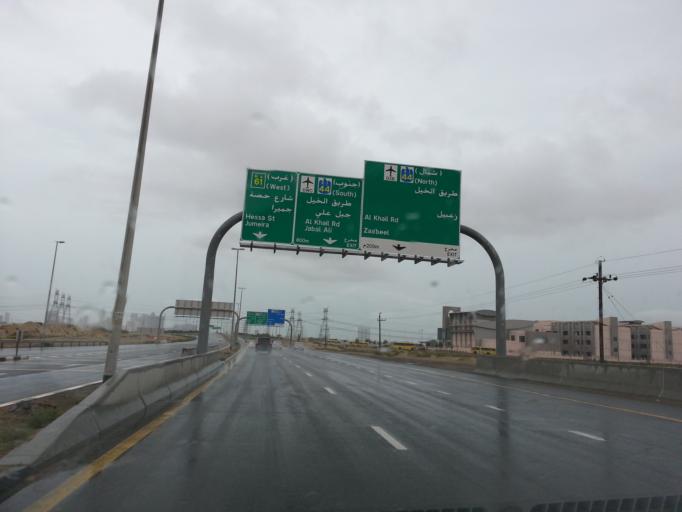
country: AE
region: Dubai
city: Dubai
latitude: 25.0720
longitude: 55.2161
